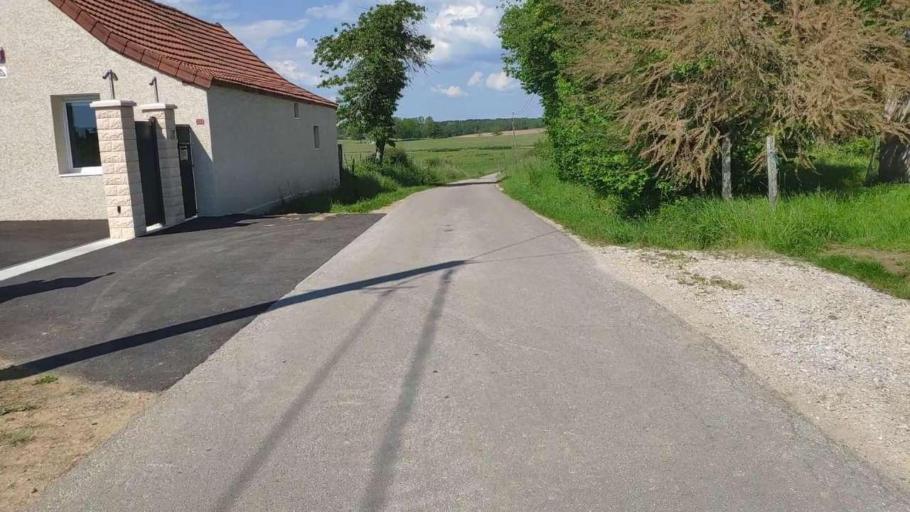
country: FR
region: Franche-Comte
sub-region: Departement du Jura
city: Bletterans
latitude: 46.8145
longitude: 5.3995
